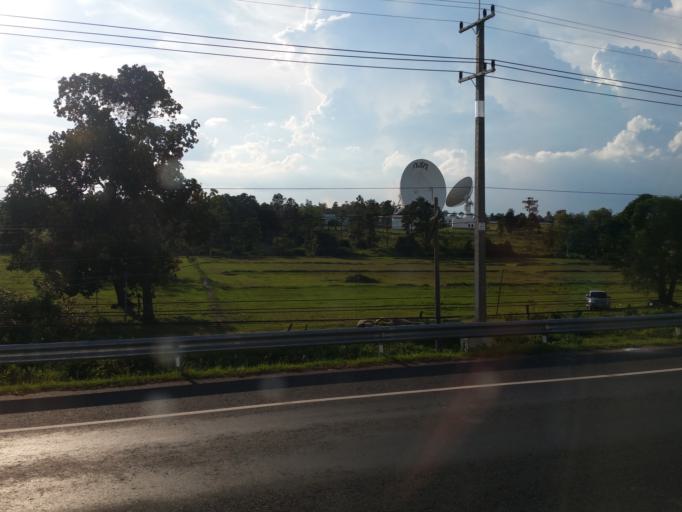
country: TH
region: Changwat Ubon Ratchathani
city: Sirindhorn
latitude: 15.1924
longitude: 105.3680
